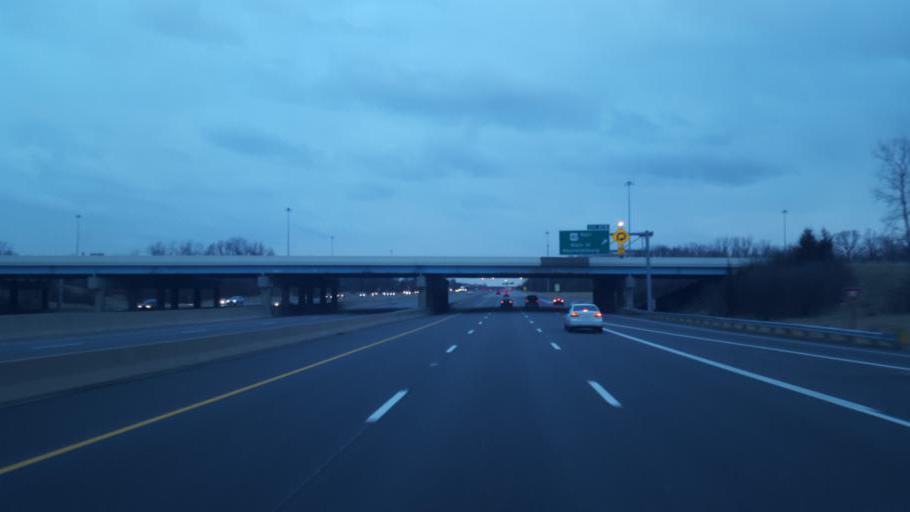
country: US
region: Ohio
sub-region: Franklin County
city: Reynoldsburg
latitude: 39.9556
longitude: -82.8445
